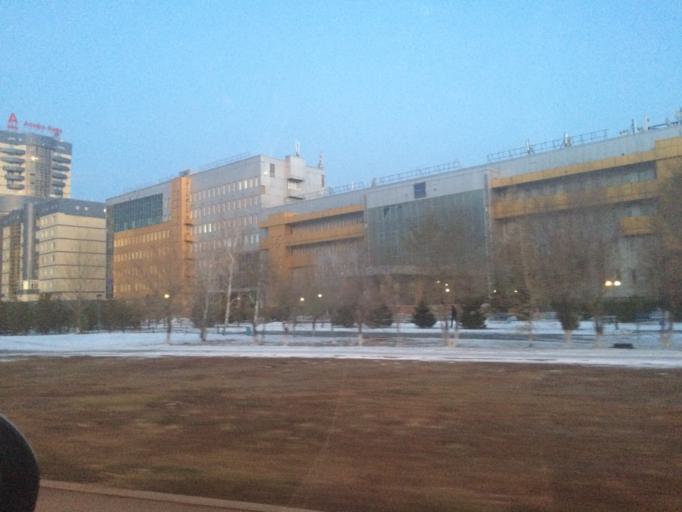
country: KZ
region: Astana Qalasy
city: Astana
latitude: 51.1450
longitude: 71.4211
